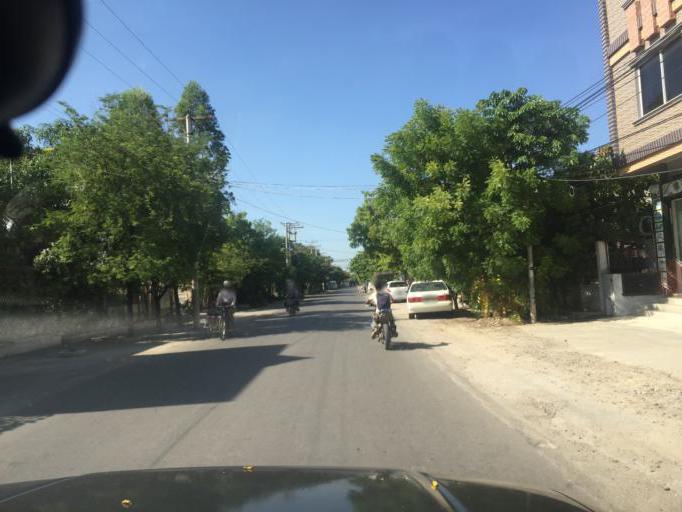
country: MM
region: Mandalay
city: Mandalay
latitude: 21.9541
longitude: 96.1098
